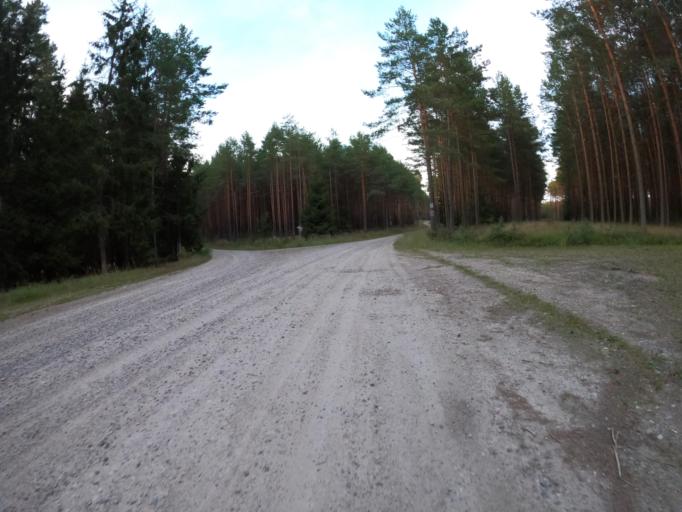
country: PL
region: West Pomeranian Voivodeship
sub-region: Powiat koszalinski
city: Sianow
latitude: 54.1019
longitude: 16.4051
